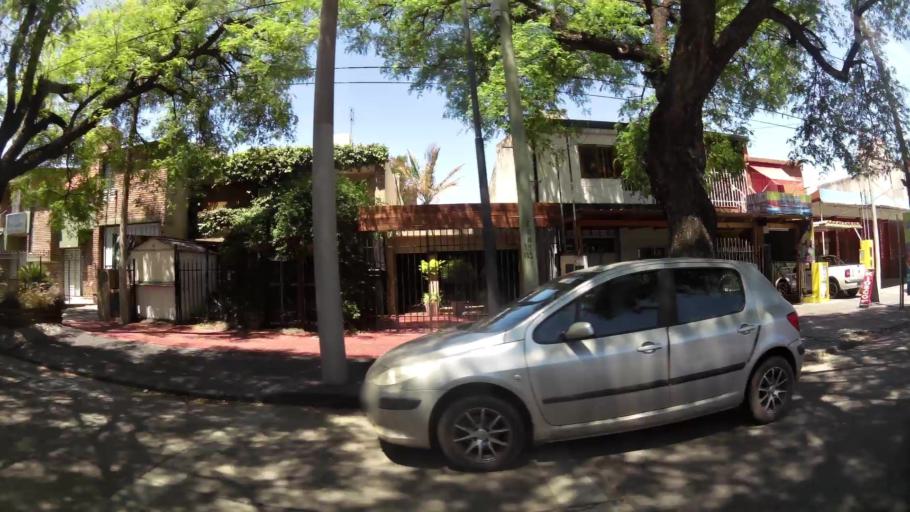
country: AR
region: Cordoba
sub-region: Departamento de Capital
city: Cordoba
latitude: -31.3789
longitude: -64.2072
